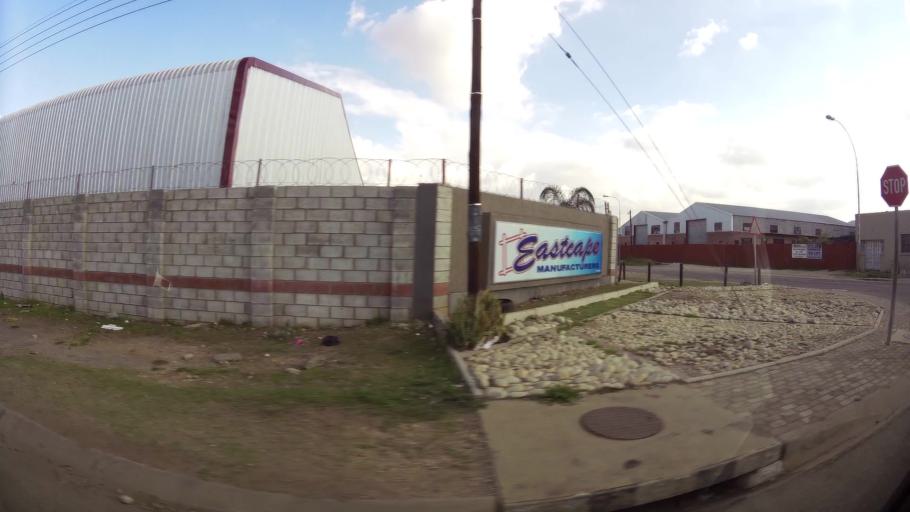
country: ZA
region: Eastern Cape
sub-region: Nelson Mandela Bay Metropolitan Municipality
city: Uitenhage
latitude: -33.7735
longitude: 25.3923
